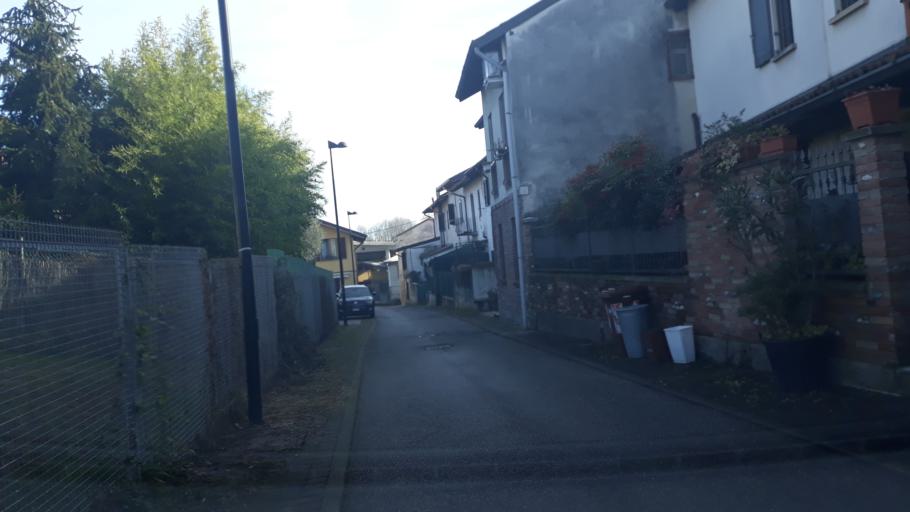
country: IT
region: Lombardy
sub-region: Provincia di Monza e Brianza
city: Aicurzio
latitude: 45.6327
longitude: 9.4092
